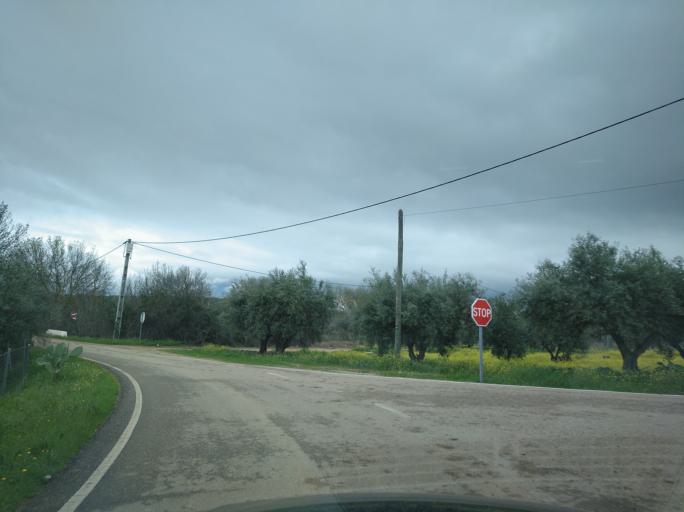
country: PT
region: Portalegre
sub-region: Campo Maior
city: Campo Maior
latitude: 38.9959
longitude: -7.0498
